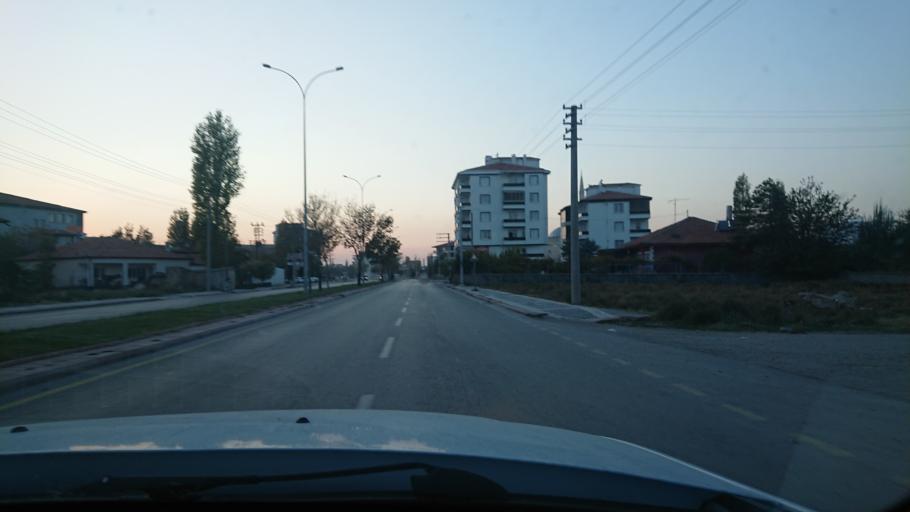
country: TR
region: Aksaray
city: Aksaray
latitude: 38.3603
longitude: 34.0042
